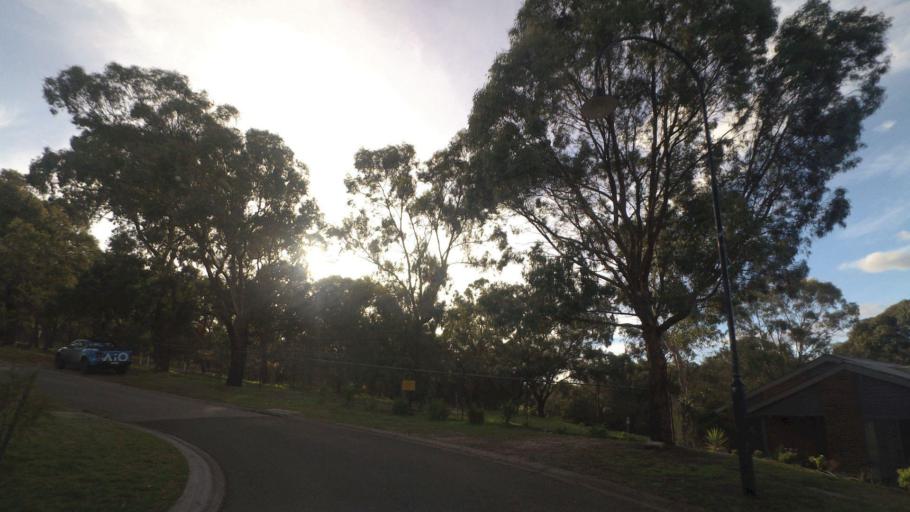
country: AU
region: Victoria
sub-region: Banyule
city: Yallambie
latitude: -37.7255
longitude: 145.0991
